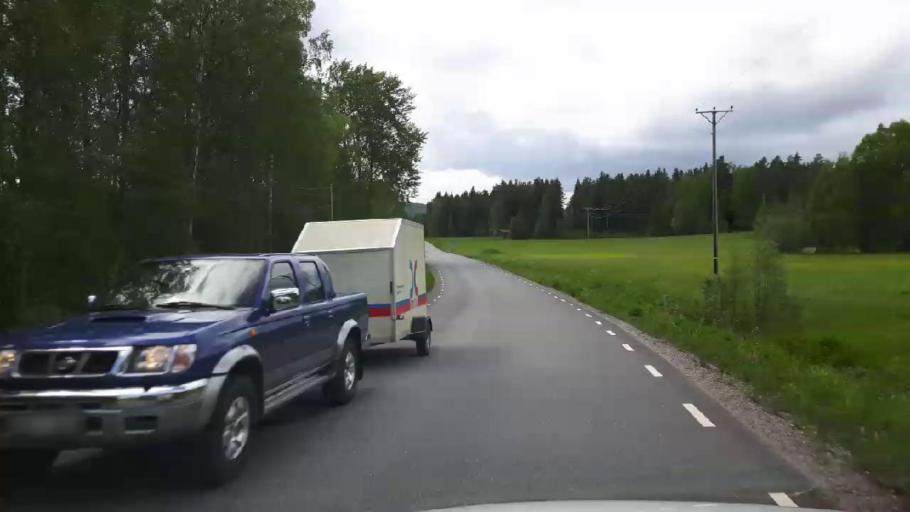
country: SE
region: Dalarna
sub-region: Faluns Kommun
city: Falun
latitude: 60.6820
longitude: 15.7663
